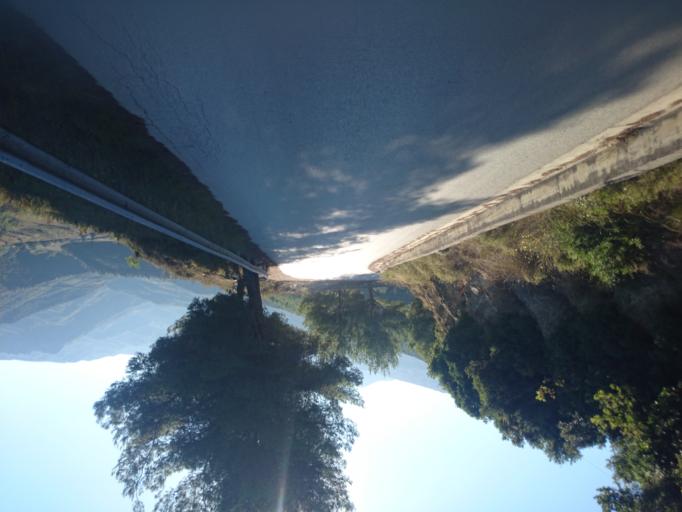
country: AL
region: Berat
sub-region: Rrethi i Beratit
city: Polican
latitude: 40.5830
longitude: 20.1101
